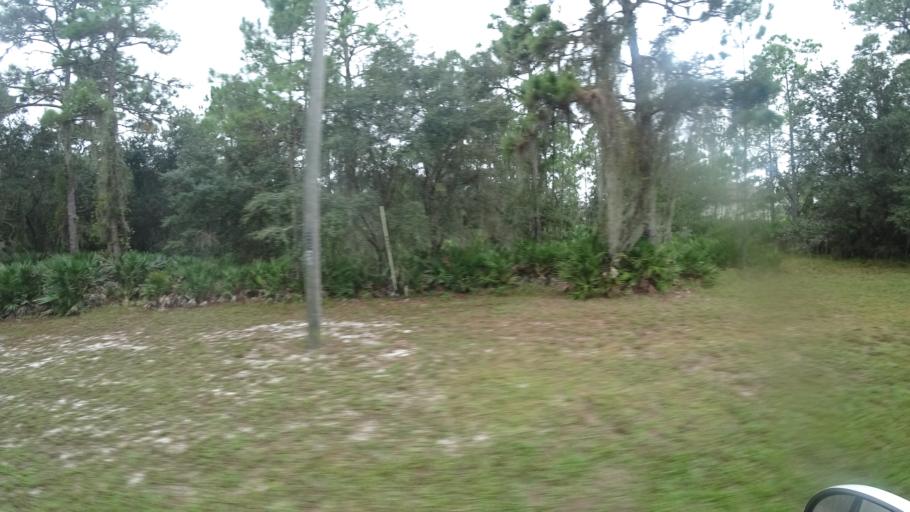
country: US
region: Florida
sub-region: Sarasota County
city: The Meadows
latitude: 27.3966
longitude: -82.3285
